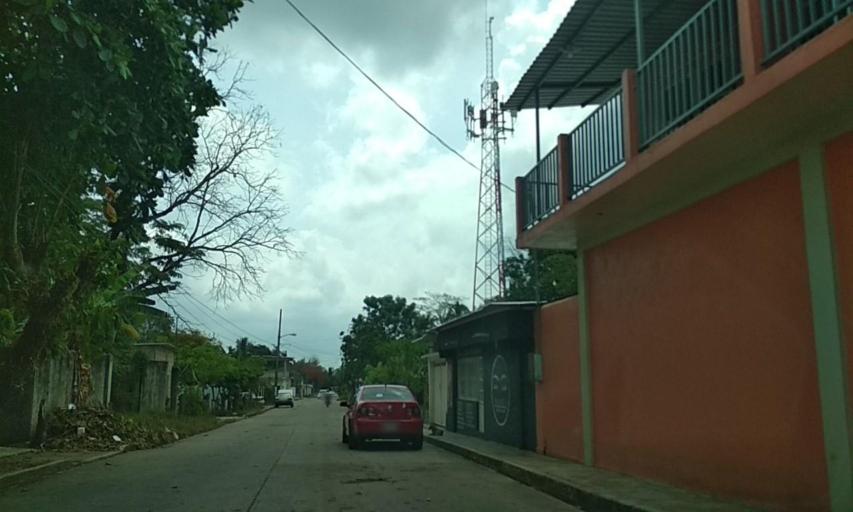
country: MX
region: Veracruz
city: Las Choapas
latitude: 17.9014
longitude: -94.1065
